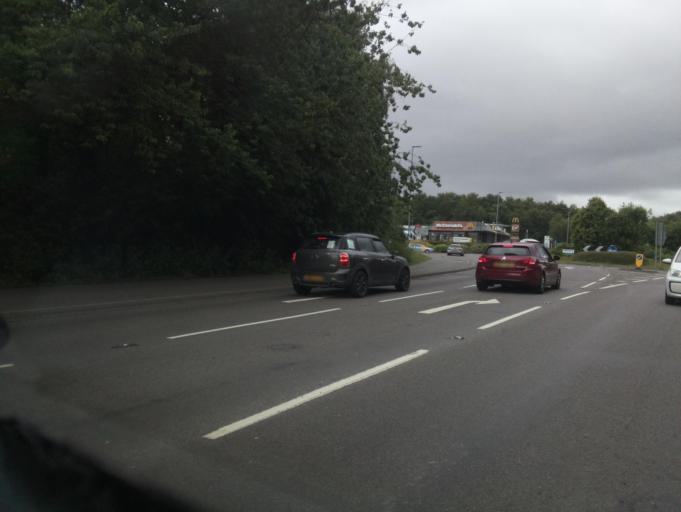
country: GB
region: England
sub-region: Leicestershire
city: Coalville
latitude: 52.7325
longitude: -1.3731
